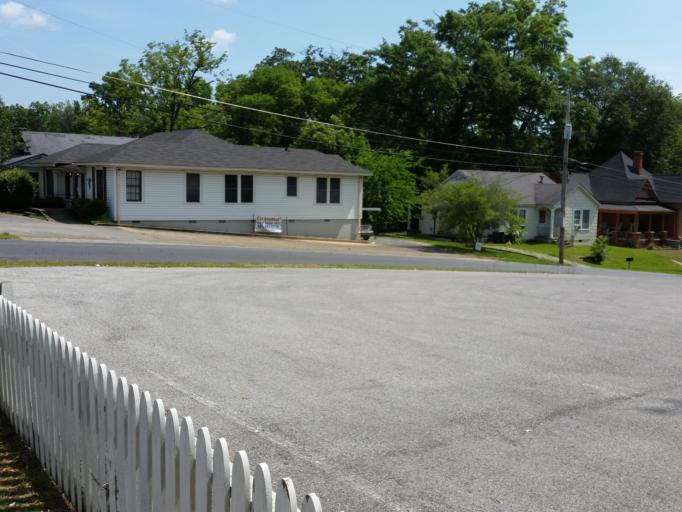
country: US
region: Mississippi
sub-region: Lauderdale County
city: Meridian
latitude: 32.3764
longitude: -88.7013
